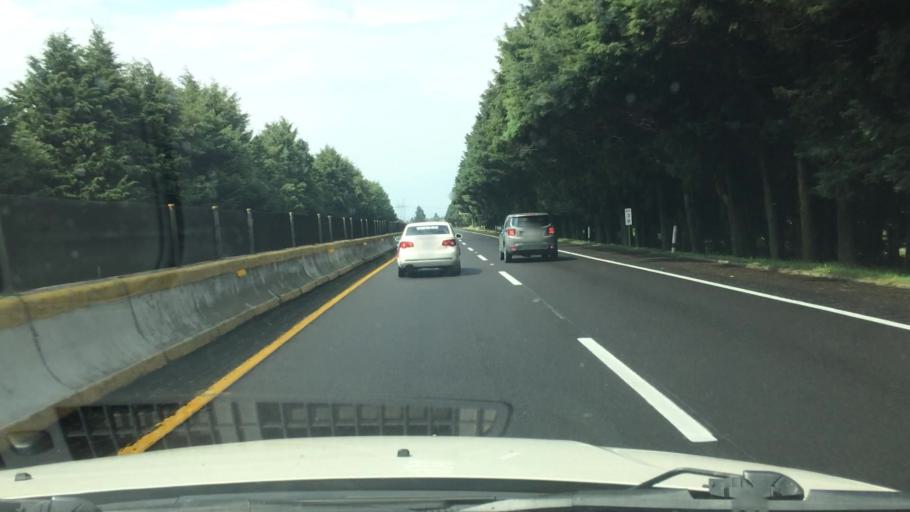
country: MX
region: Mexico City
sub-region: Tlalpan
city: Lomas de Tepemecatl
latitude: 19.1475
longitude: -99.1609
